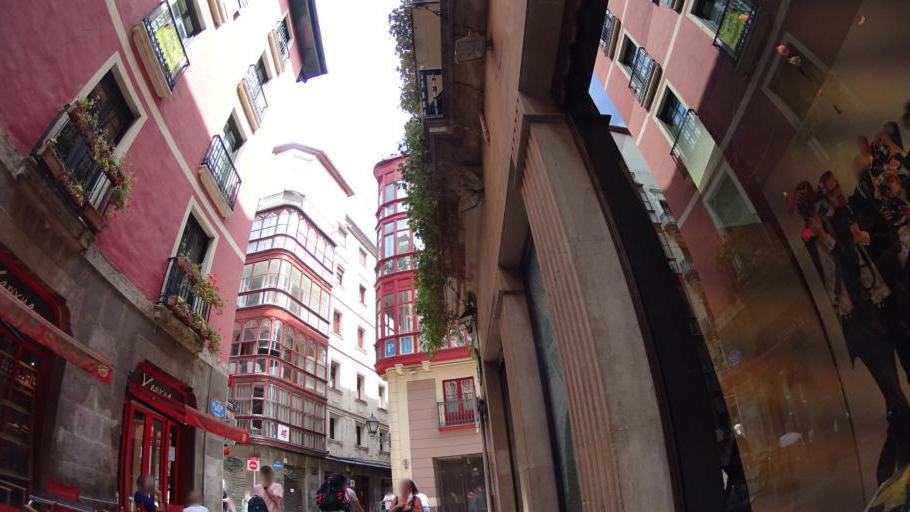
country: ES
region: Basque Country
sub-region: Bizkaia
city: Bilbao
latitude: 43.2585
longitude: -2.9236
